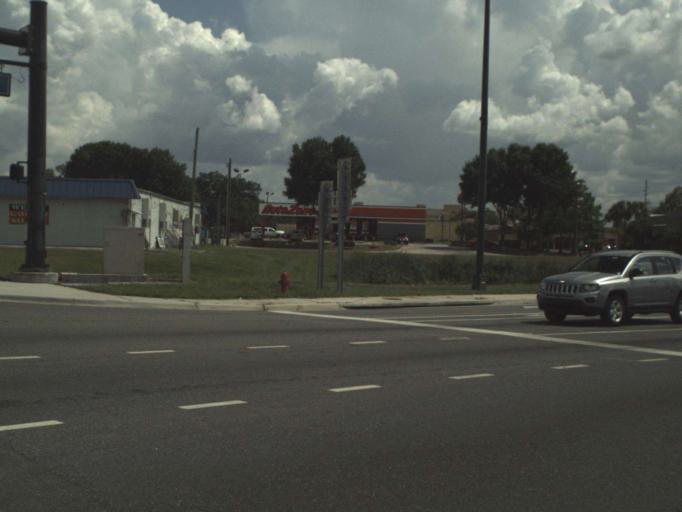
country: US
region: Florida
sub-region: Lake County
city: Leesburg
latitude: 28.8255
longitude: -81.8864
